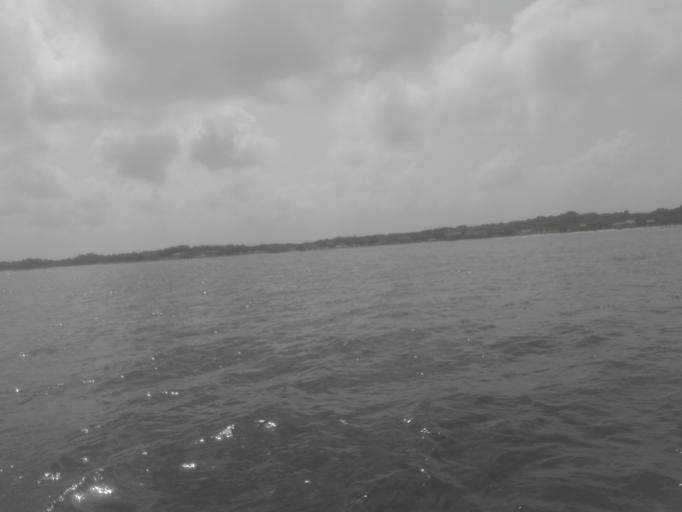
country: CO
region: Bolivar
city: Turbana
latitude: 10.2290
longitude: -75.6109
